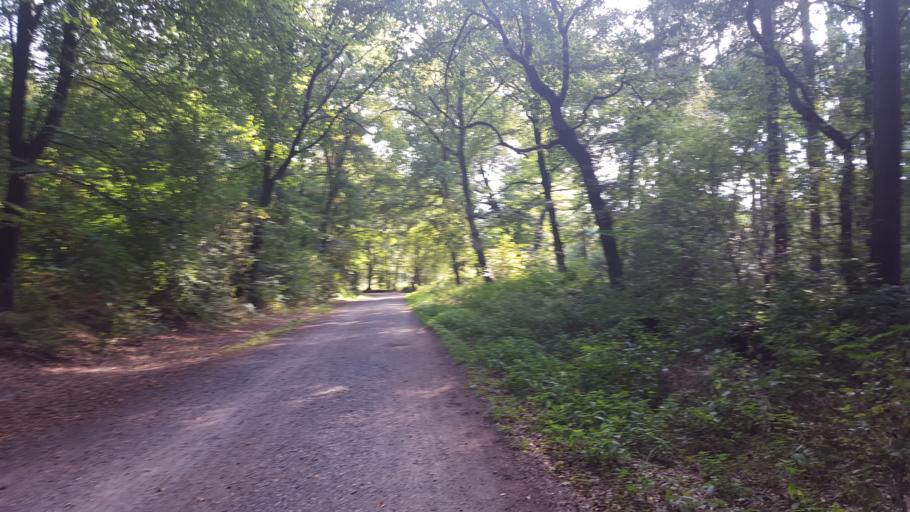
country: DE
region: North Rhine-Westphalia
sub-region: Regierungsbezirk Munster
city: Haltern
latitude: 51.7098
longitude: 7.2266
